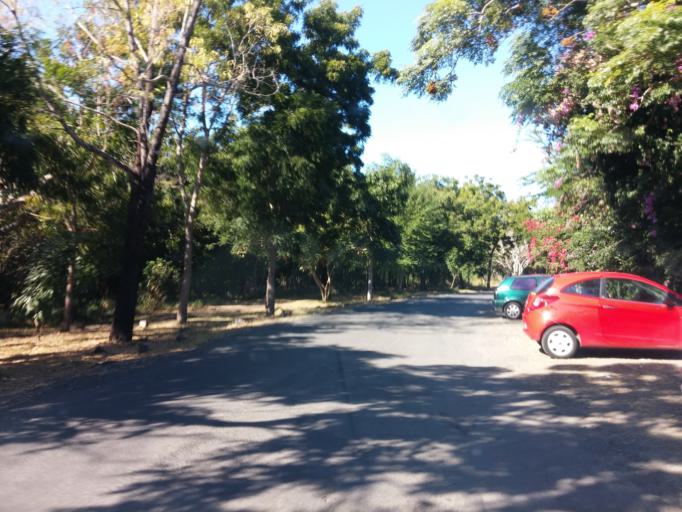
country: RE
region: Reunion
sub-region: Reunion
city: Les Avirons
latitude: -21.2681
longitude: 55.3536
